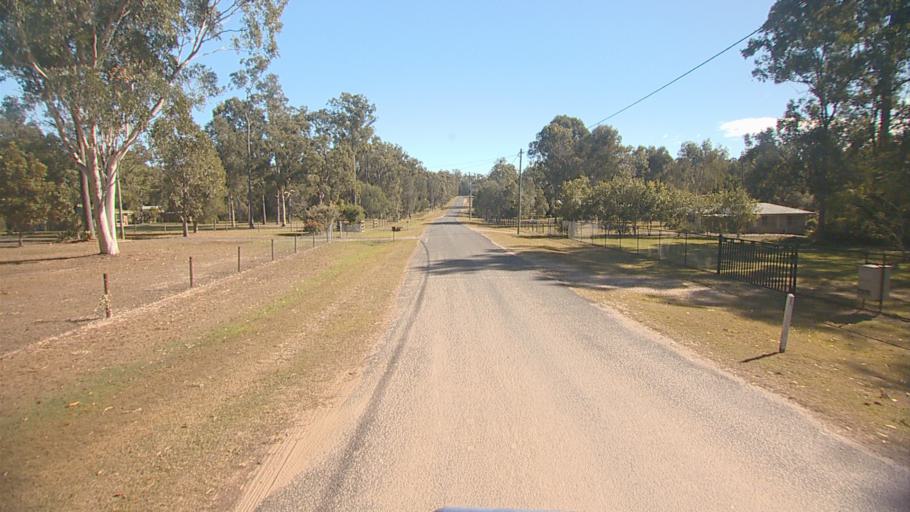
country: AU
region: Queensland
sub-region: Logan
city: Chambers Flat
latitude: -27.7797
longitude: 153.0786
